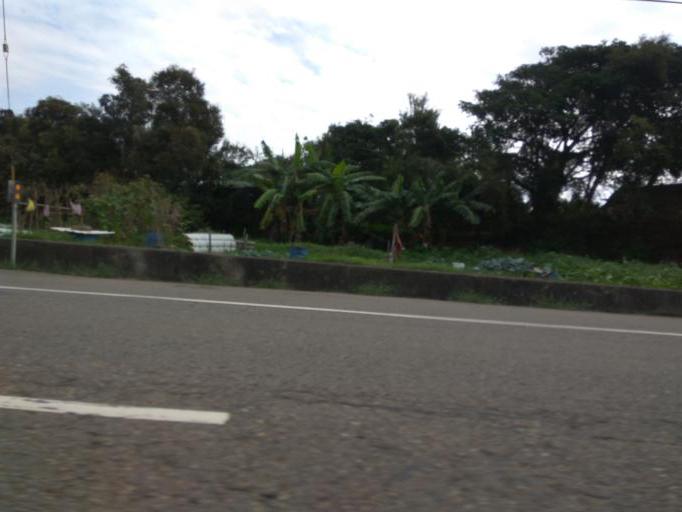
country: TW
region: Taiwan
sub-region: Hsinchu
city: Zhubei
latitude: 24.9639
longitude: 121.0149
